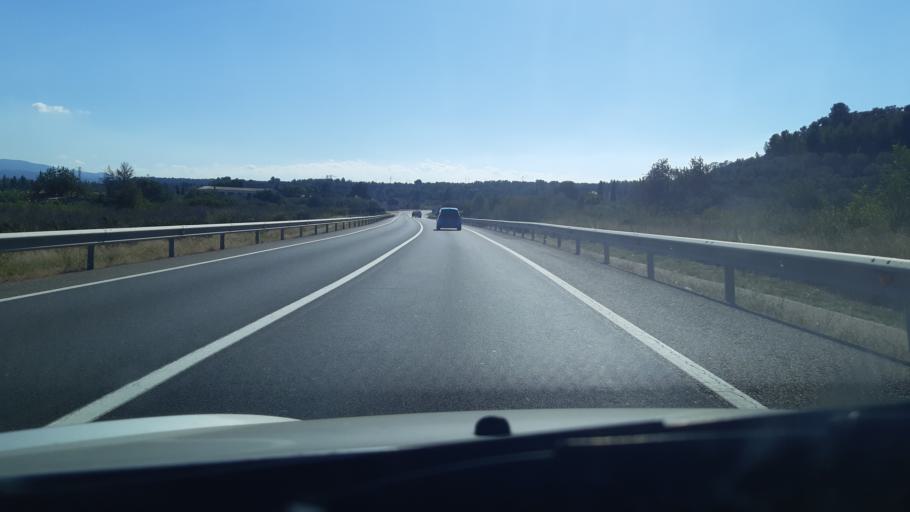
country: ES
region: Catalonia
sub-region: Provincia de Tarragona
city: Tivenys
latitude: 40.9082
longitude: 0.4832
